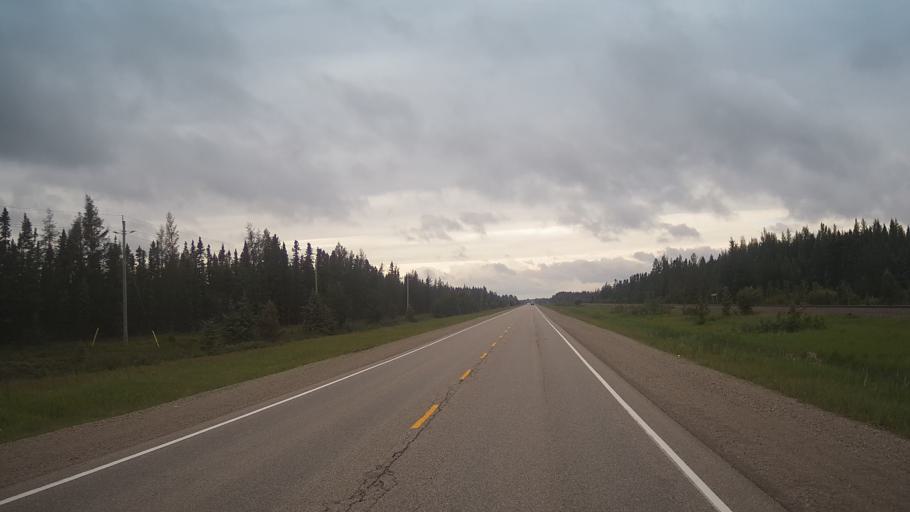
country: CA
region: Ontario
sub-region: Thunder Bay District
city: Thunder Bay
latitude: 48.8574
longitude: -89.9595
